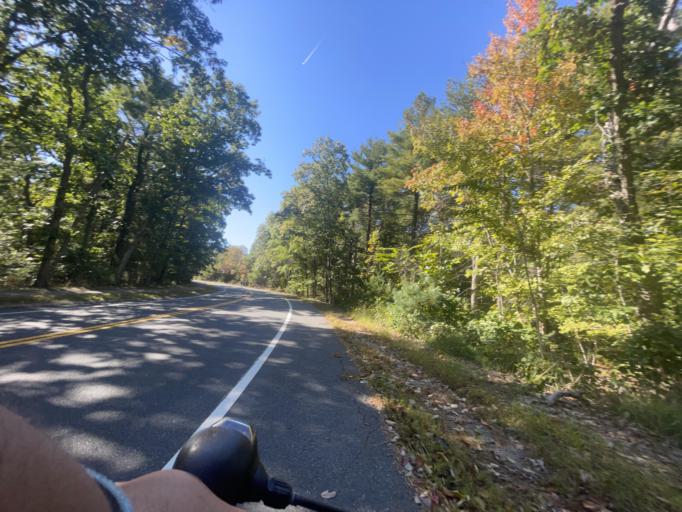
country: US
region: Massachusetts
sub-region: Norfolk County
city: Milton
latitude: 42.2358
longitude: -71.0353
